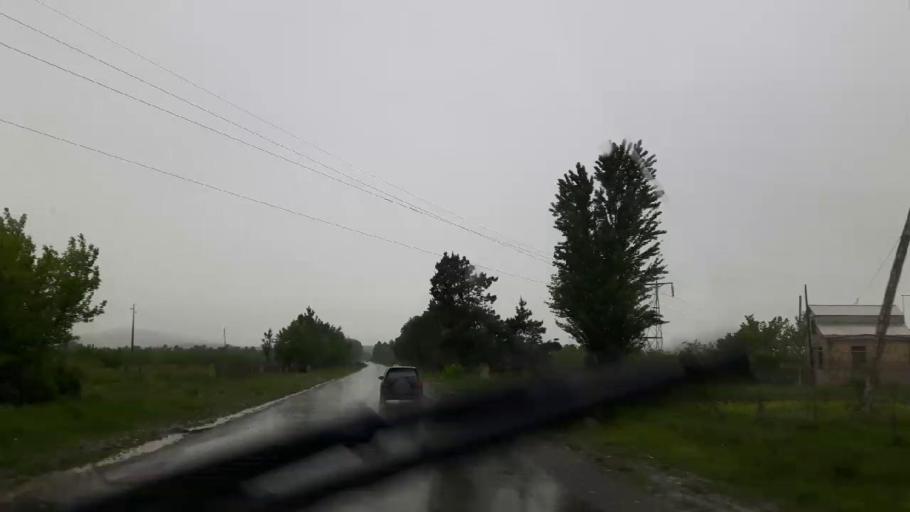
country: GE
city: Agara
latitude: 42.0122
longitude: 43.8608
